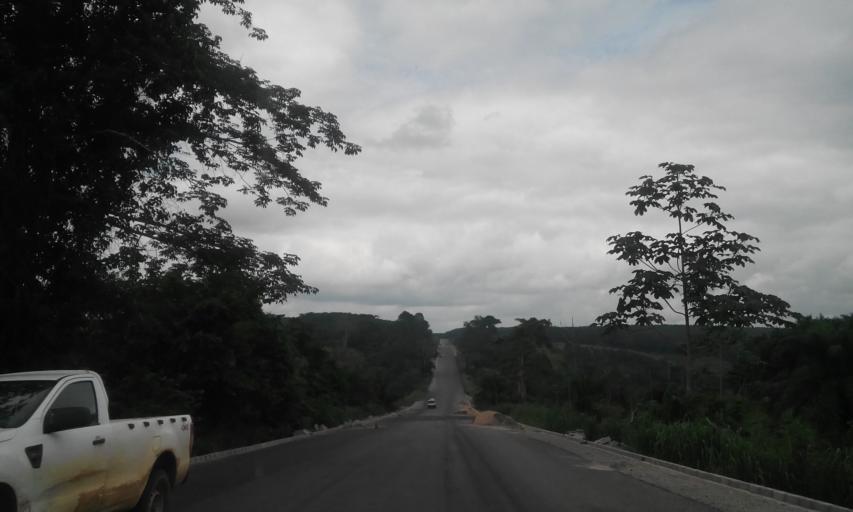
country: CI
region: Sud-Comoe
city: Mafere
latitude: 5.3111
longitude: -3.0477
